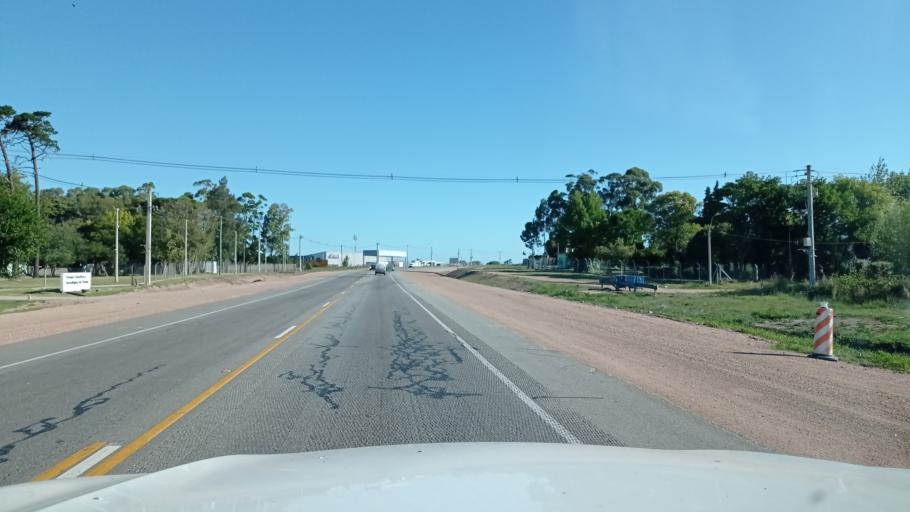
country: UY
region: Canelones
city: Pando
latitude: -34.7202
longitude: -55.9491
